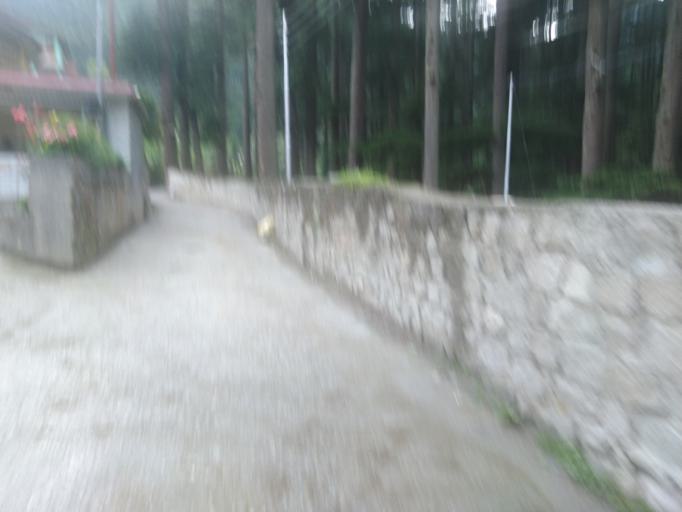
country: IN
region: Himachal Pradesh
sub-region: Kulu
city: Manali
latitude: 32.2467
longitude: 77.1786
